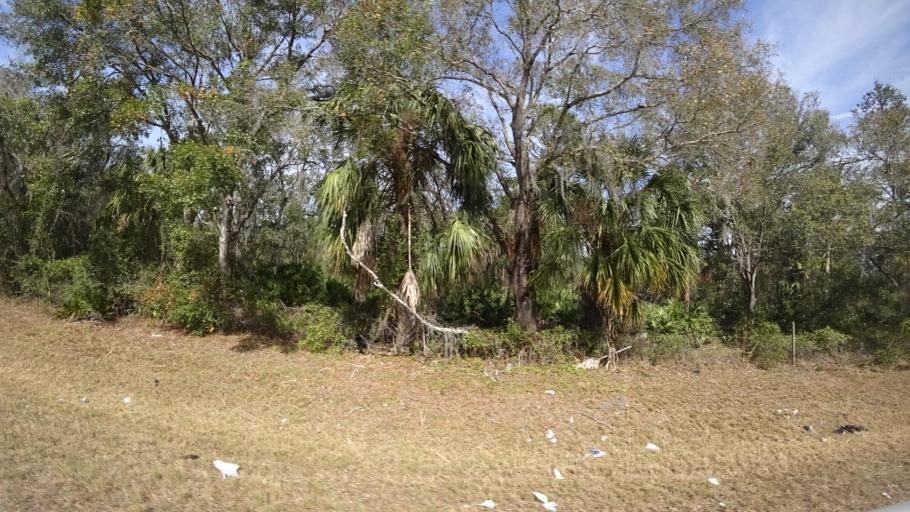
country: US
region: Florida
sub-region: Manatee County
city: Ellenton
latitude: 27.5136
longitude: -82.3774
